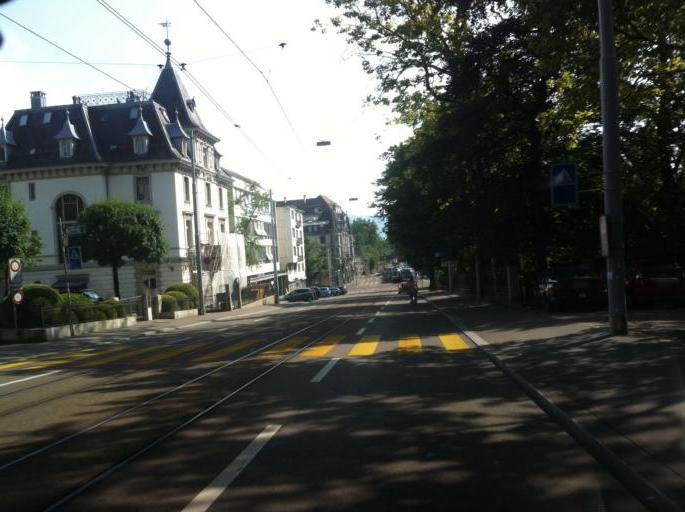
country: CH
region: Zurich
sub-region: Bezirk Zuerich
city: Zurich
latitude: 47.3719
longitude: 8.5506
